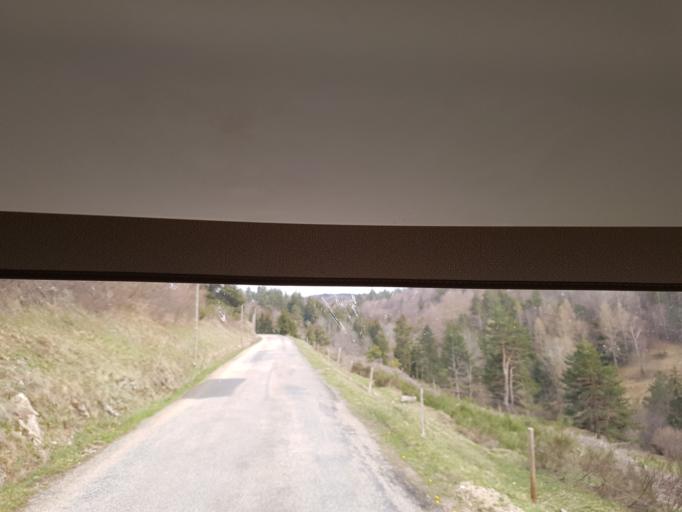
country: FR
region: Languedoc-Roussillon
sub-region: Departement de l'Aude
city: Quillan
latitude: 42.6884
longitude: 2.1043
